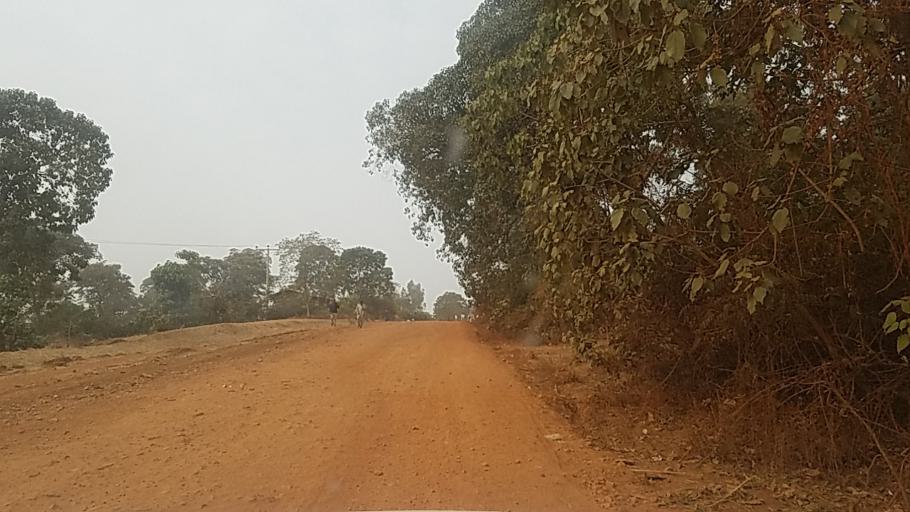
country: ET
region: Amhara
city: Bure
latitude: 10.8566
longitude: 36.3587
